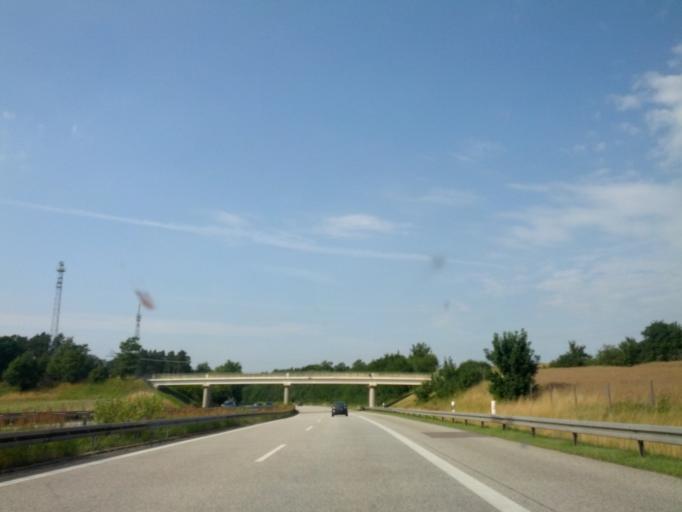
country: DE
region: Mecklenburg-Vorpommern
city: Lalendorf
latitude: 53.7200
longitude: 12.3573
